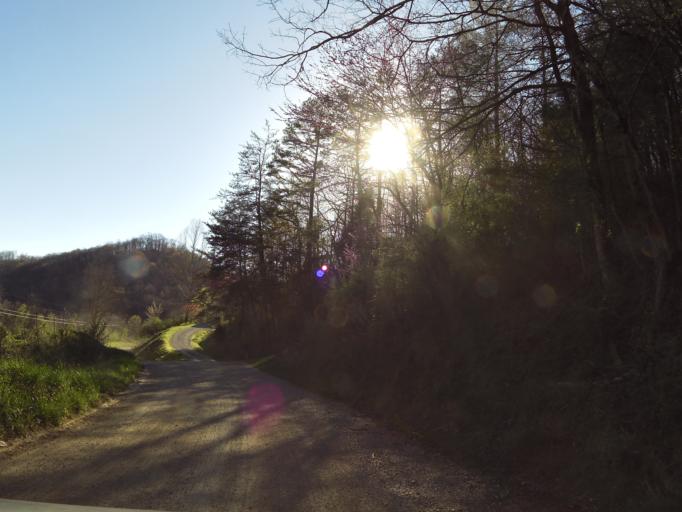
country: US
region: Tennessee
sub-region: Campbell County
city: Caryville
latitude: 36.2723
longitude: -84.3892
